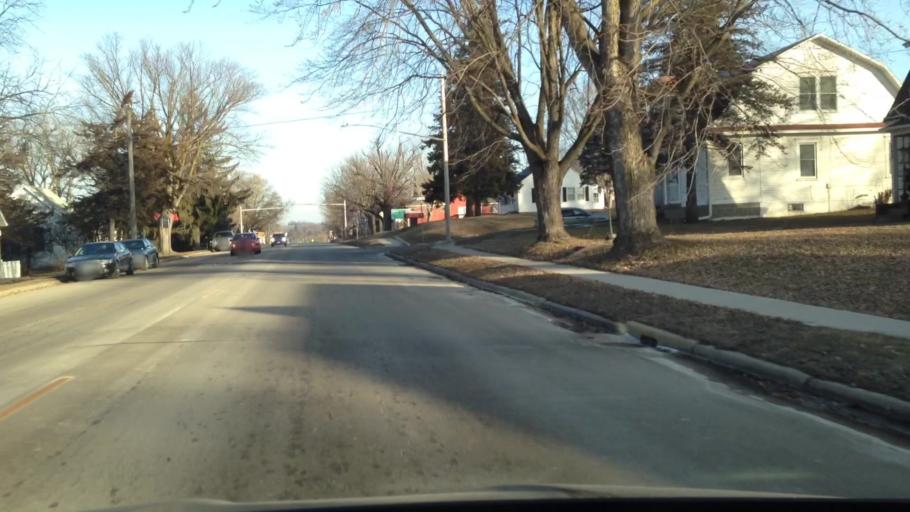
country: US
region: Minnesota
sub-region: Goodhue County
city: Zumbrota
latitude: 44.2894
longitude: -92.6691
